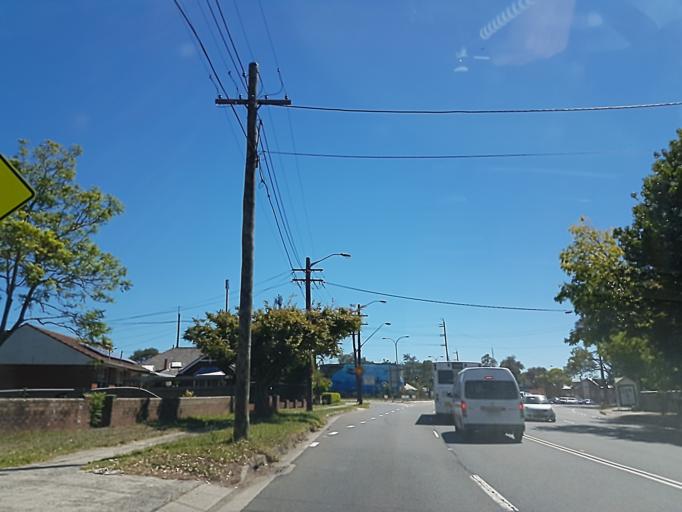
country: AU
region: New South Wales
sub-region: Hornsby Shire
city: Asquith
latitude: -33.6922
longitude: 151.0983
